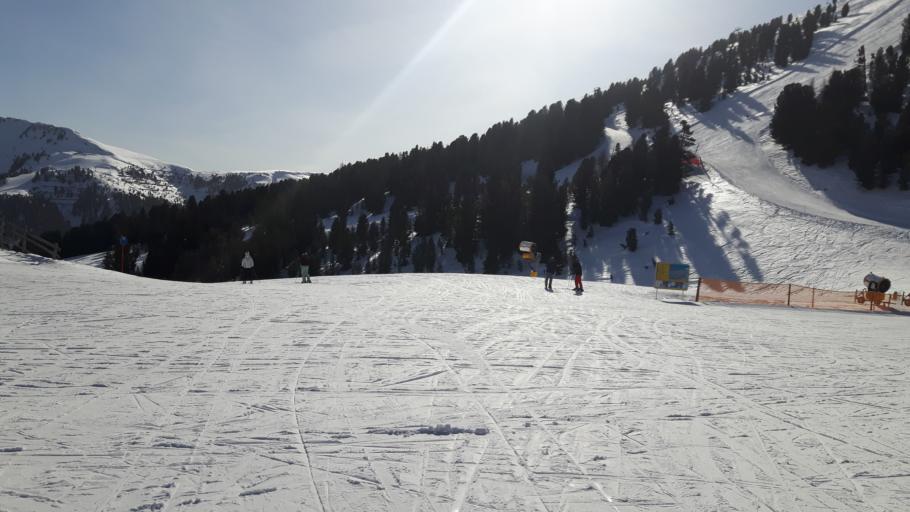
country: IT
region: Trentino-Alto Adige
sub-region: Provincia di Trento
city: Panchia
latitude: 46.3535
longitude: 11.5367
